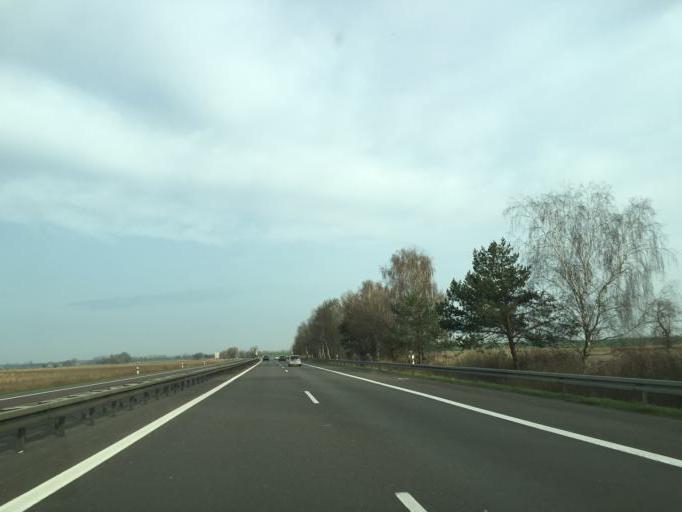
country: DE
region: Brandenburg
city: Kremmen
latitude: 52.7372
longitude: 12.9171
